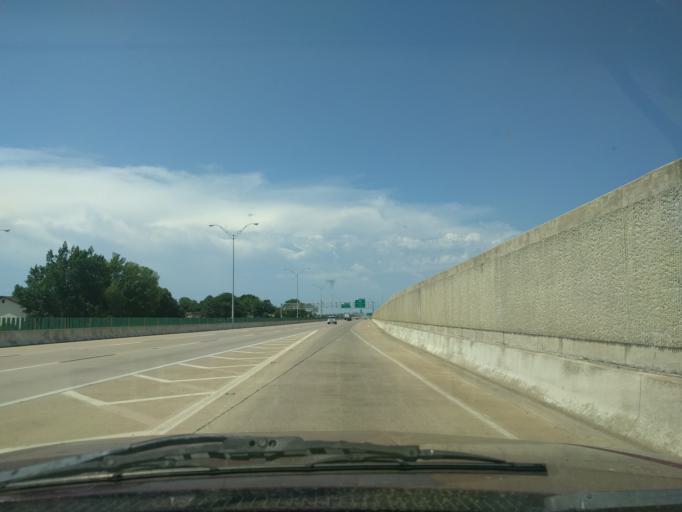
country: US
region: Oklahoma
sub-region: Tulsa County
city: Broken Arrow
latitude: 36.1445
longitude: -95.8531
